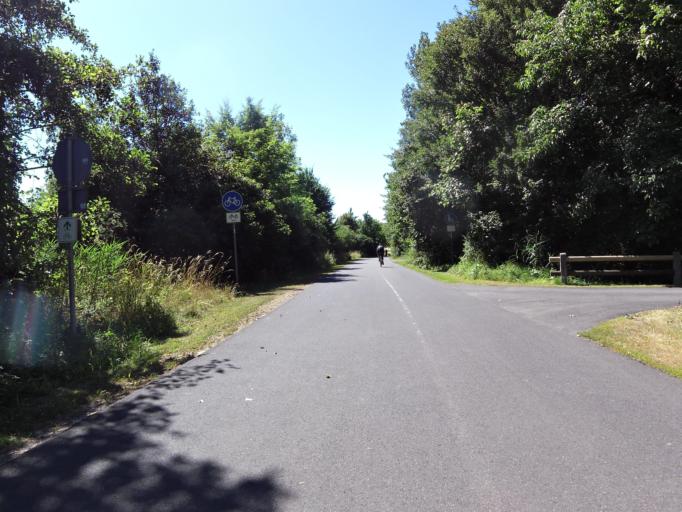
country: DE
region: Bavaria
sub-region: Regierungsbezirk Unterfranken
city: Randersacker
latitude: 49.7491
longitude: 9.9870
